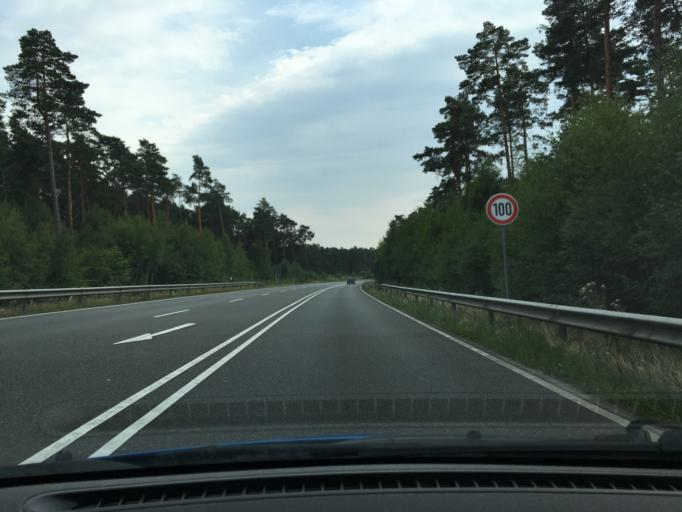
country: DE
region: Lower Saxony
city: Adelheidsdorf
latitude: 52.5702
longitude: 10.0780
